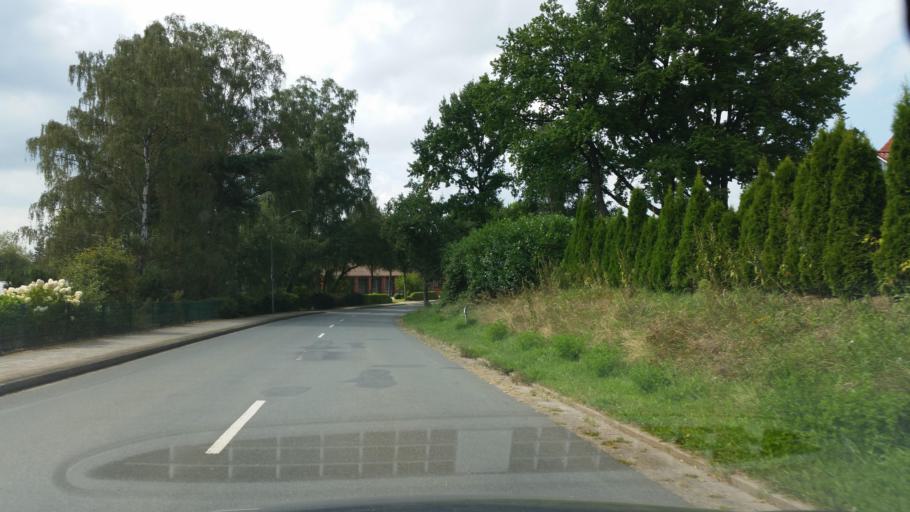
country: DE
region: Lower Saxony
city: Neuenkirchen
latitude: 53.0376
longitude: 9.7124
